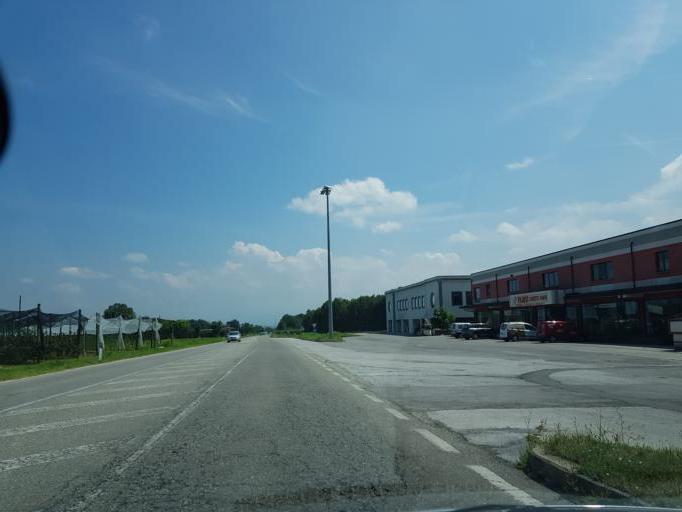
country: IT
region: Piedmont
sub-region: Provincia di Cuneo
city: Montemale di Cuneo
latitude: 44.4466
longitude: 7.4001
